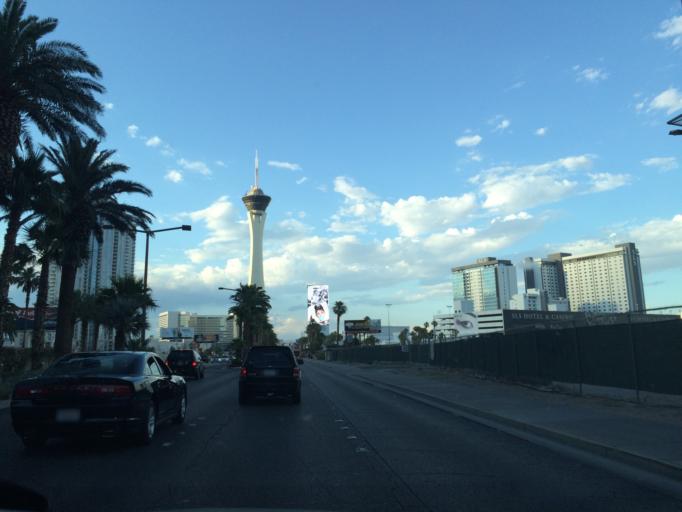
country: US
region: Nevada
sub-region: Clark County
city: Winchester
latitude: 36.1393
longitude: -115.1601
